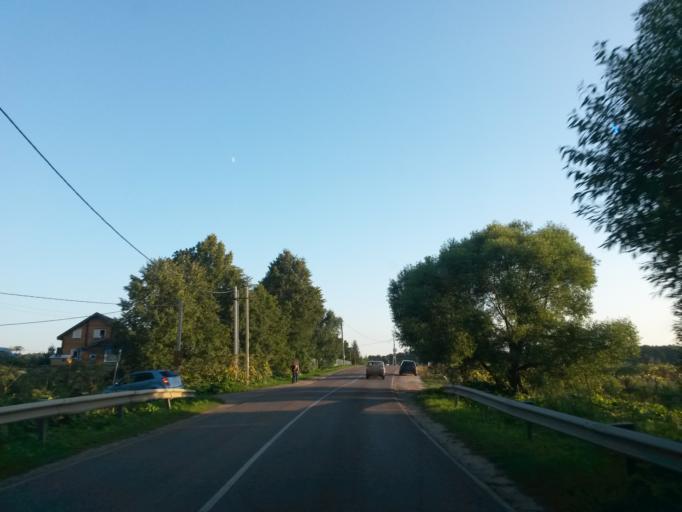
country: RU
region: Moskovskaya
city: Belyye Stolby
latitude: 55.2660
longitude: 37.7668
